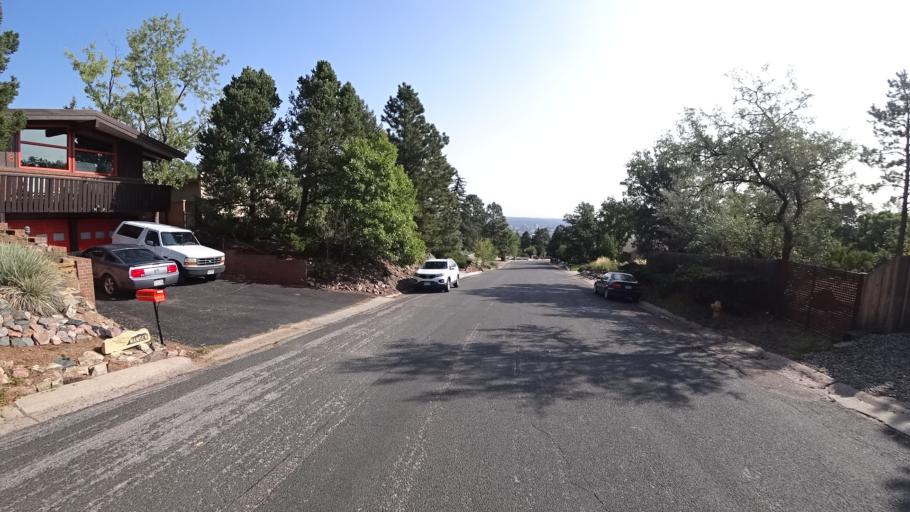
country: US
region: Colorado
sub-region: El Paso County
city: Colorado Springs
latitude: 38.8162
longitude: -104.8683
